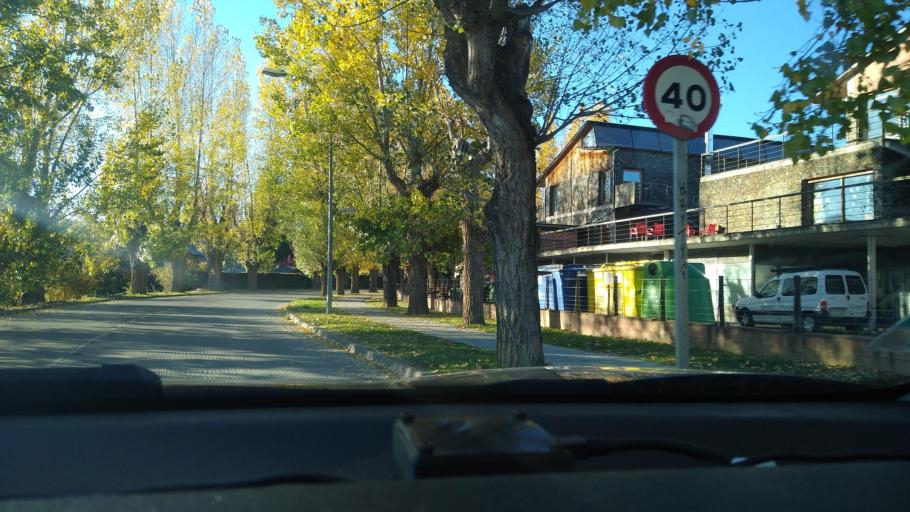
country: ES
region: Catalonia
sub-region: Provincia de Girona
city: Puigcerda
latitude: 42.4378
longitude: 1.9327
